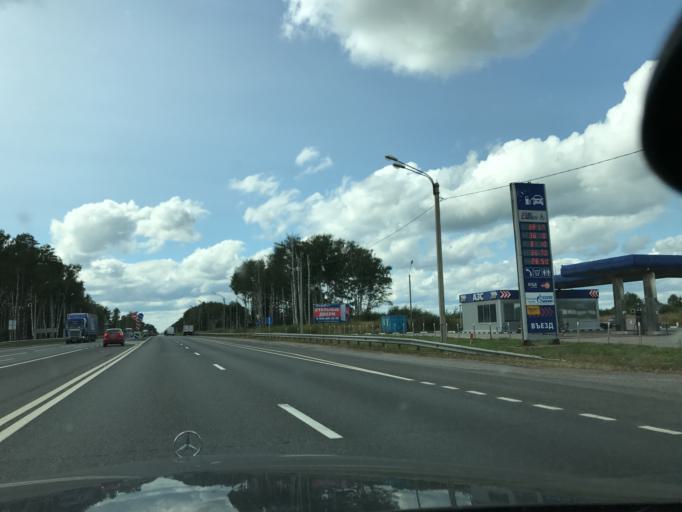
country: RU
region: Vladimir
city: Nikologory
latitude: 56.2365
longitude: 41.9428
